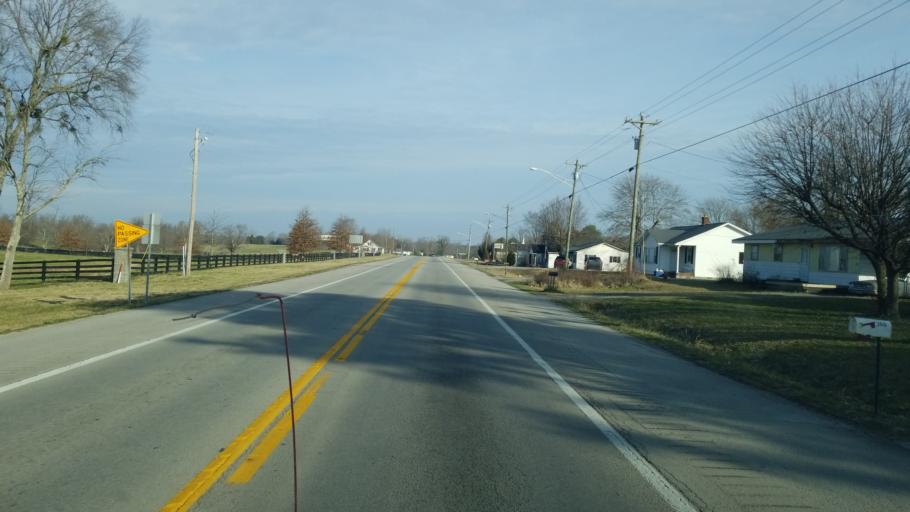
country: US
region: Kentucky
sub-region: Russell County
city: Russell Springs
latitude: 37.0704
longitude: -85.0716
